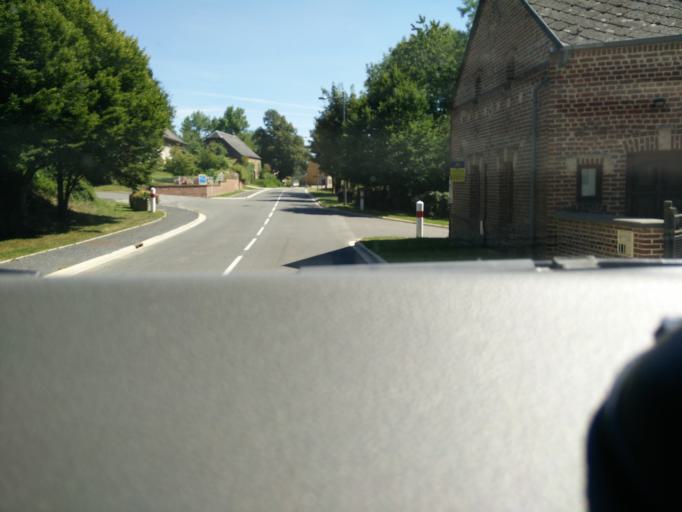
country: FR
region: Nord-Pas-de-Calais
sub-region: Departement du Nord
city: Trelon
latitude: 50.1207
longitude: 4.0964
